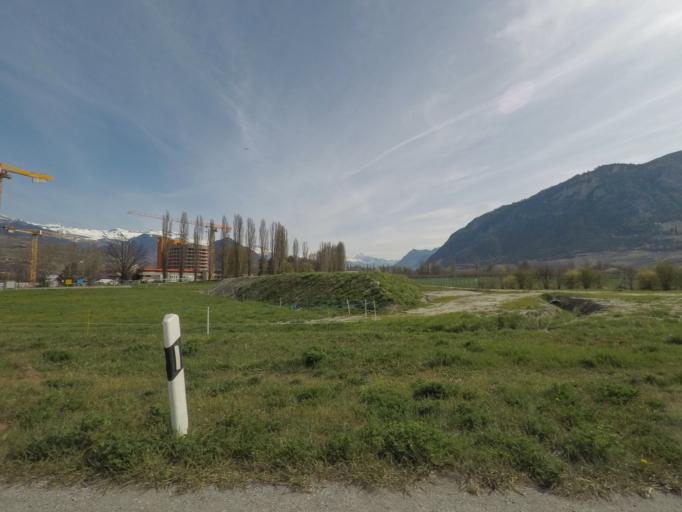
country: CH
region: Valais
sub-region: Herens District
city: Vex
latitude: 46.2321
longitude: 7.3846
